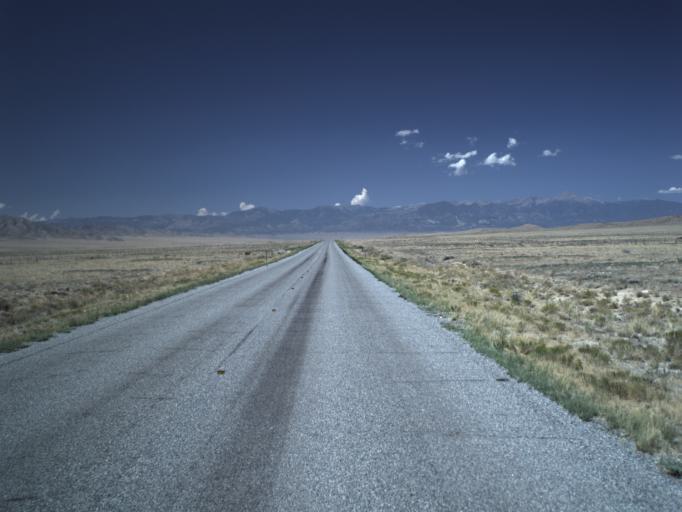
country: US
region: Utah
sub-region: Beaver County
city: Milford
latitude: 39.0634
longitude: -113.7476
